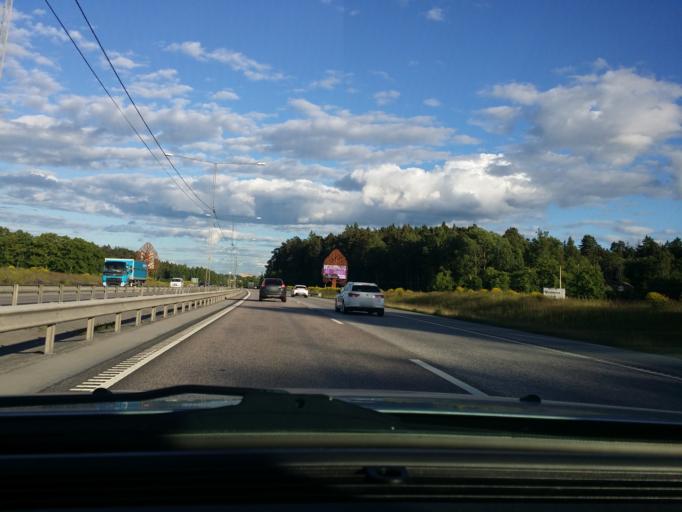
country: SE
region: Stockholm
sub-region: Upplands Vasby Kommun
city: Upplands Vaesby
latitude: 59.5359
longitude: 17.9124
